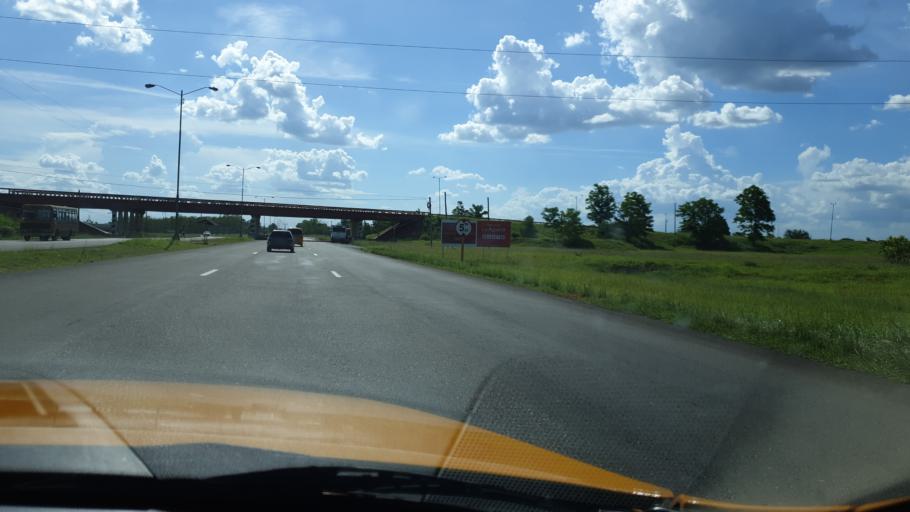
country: CU
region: Cienfuegos
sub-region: Municipio de Aguada de Pasajeros
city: Aguada de Pasajeros
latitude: 22.4035
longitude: -80.8615
